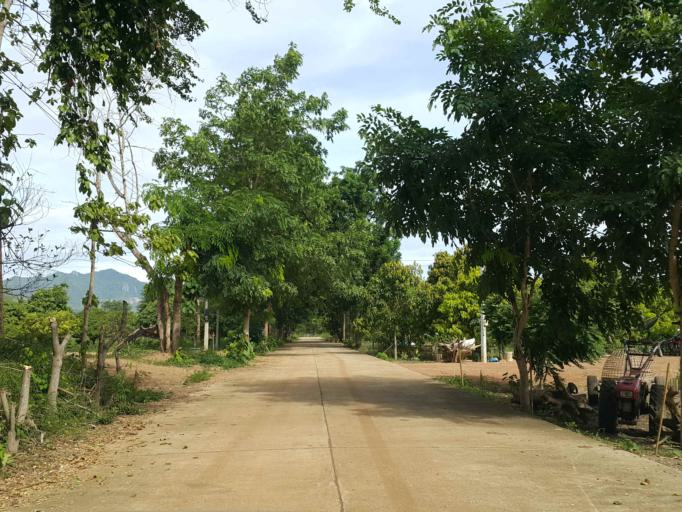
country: TH
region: Sukhothai
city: Thung Saliam
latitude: 17.2258
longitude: 99.5310
